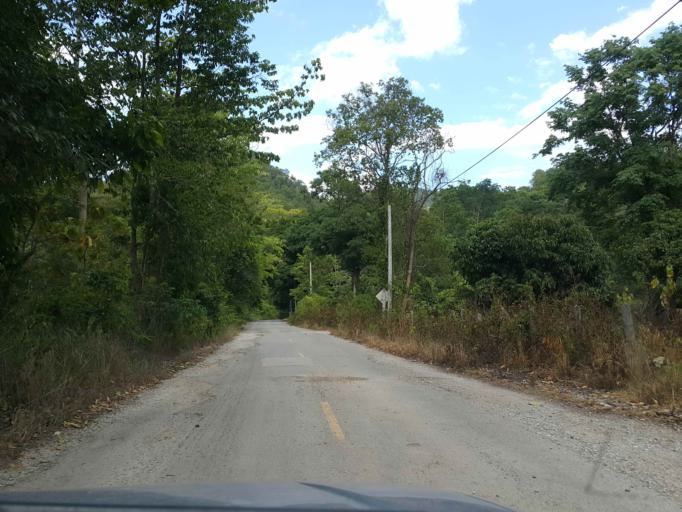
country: TH
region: Lampang
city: Thoen
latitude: 17.6472
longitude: 99.2936
